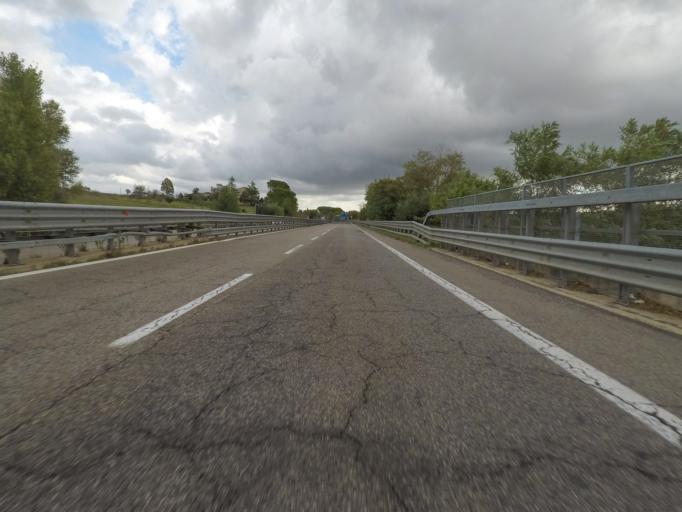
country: IT
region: Tuscany
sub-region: Provincia di Siena
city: Taverne D'Arbia
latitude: 43.2957
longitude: 11.3938
